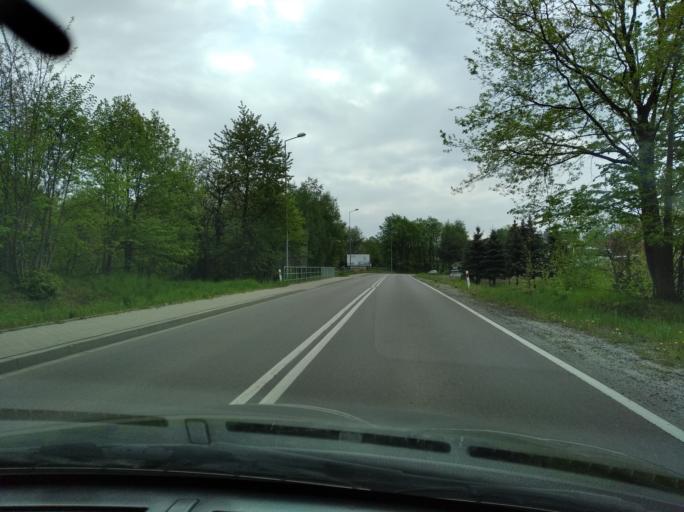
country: PL
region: Lesser Poland Voivodeship
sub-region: Powiat tarnowski
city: Tarnowiec
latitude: 49.9702
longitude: 20.9934
